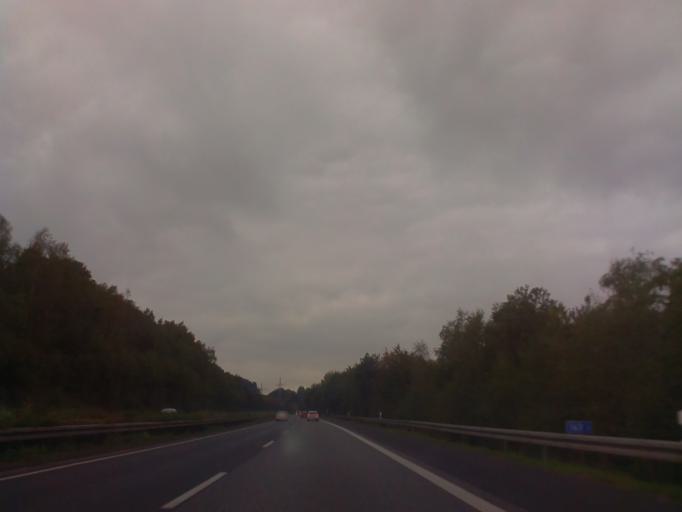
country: DE
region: Hesse
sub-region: Regierungsbezirk Darmstadt
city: Bad Orb
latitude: 50.2560
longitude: 9.3428
